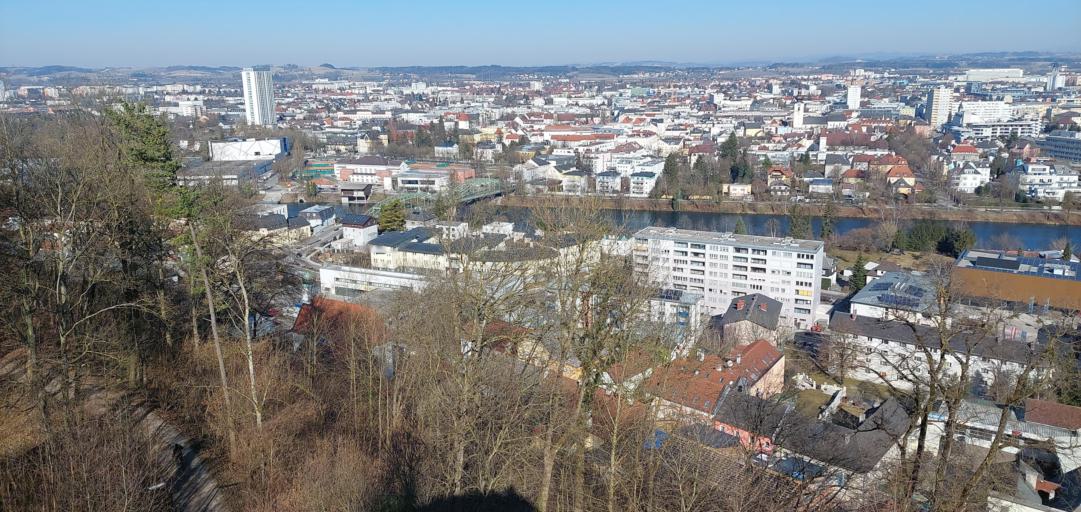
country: AT
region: Upper Austria
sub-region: Wels-Land
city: Thalheim bei Wels
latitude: 48.1507
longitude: 14.0310
